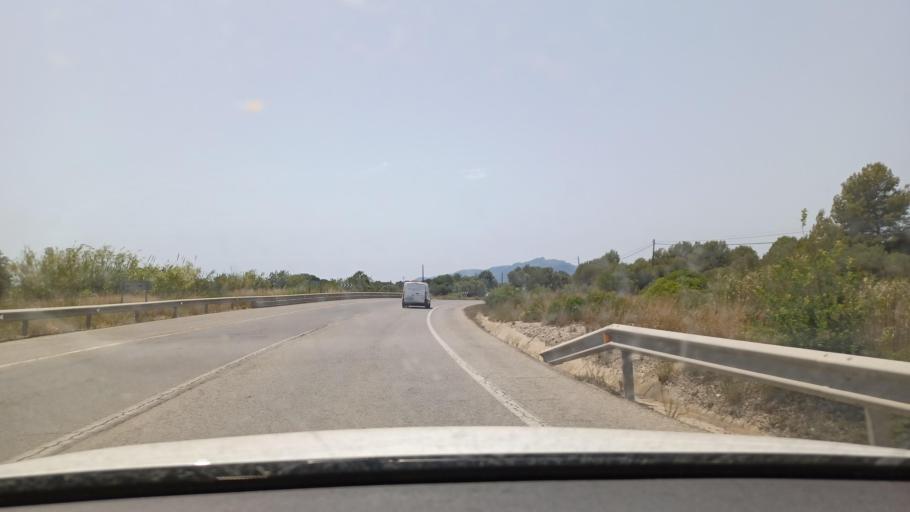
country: ES
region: Catalonia
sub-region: Provincia de Tarragona
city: Cambrils
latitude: 41.0477
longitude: 0.9972
